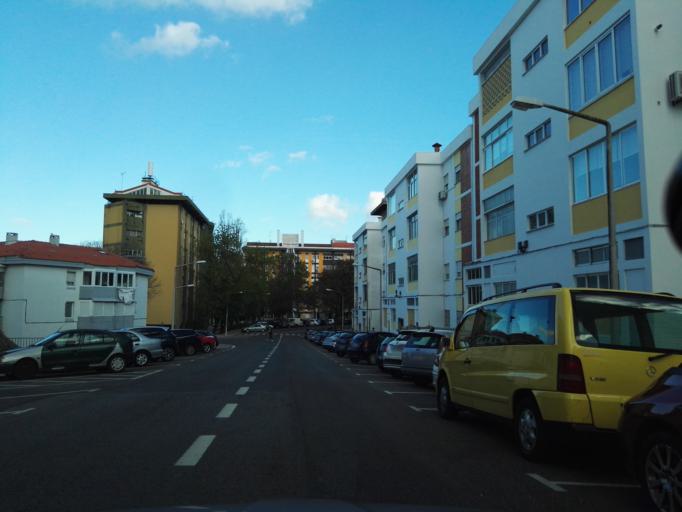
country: PT
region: Lisbon
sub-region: Loures
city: Moscavide
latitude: 38.7652
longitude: -9.1153
